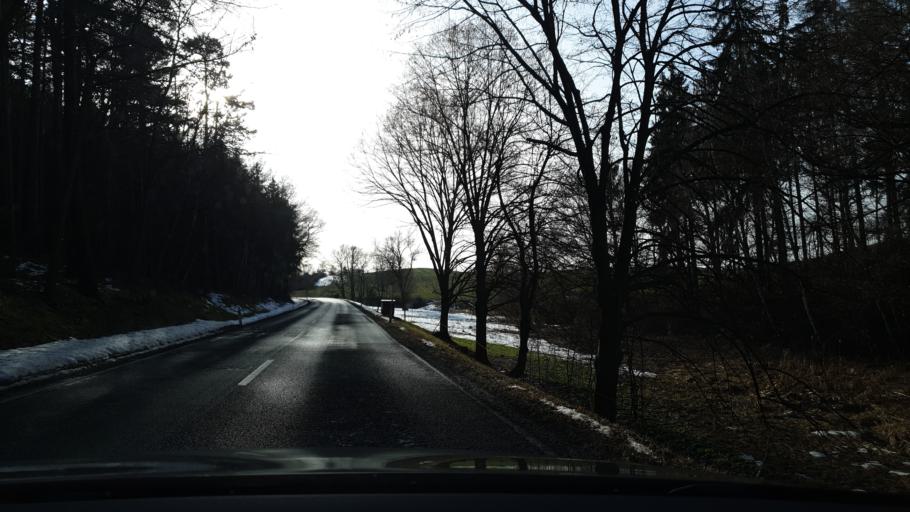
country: DE
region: Thuringia
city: Hohenleuben
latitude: 50.7227
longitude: 12.0643
